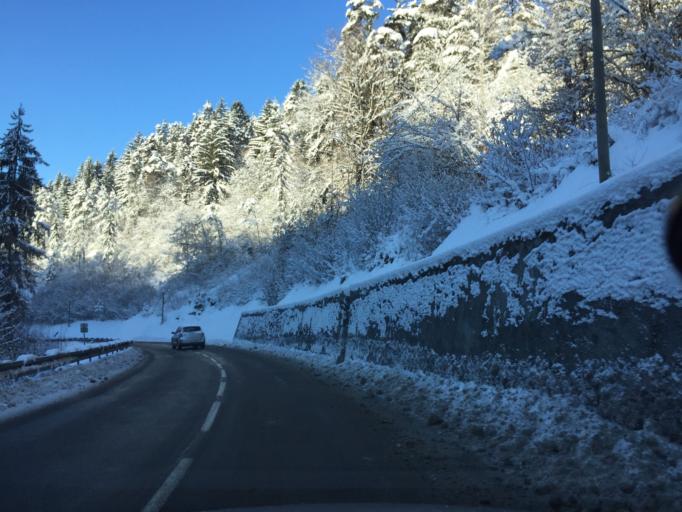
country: FR
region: Rhone-Alpes
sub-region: Departement de la Haute-Savoie
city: Saint-Paul-en-Chablais
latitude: 46.3358
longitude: 6.6330
